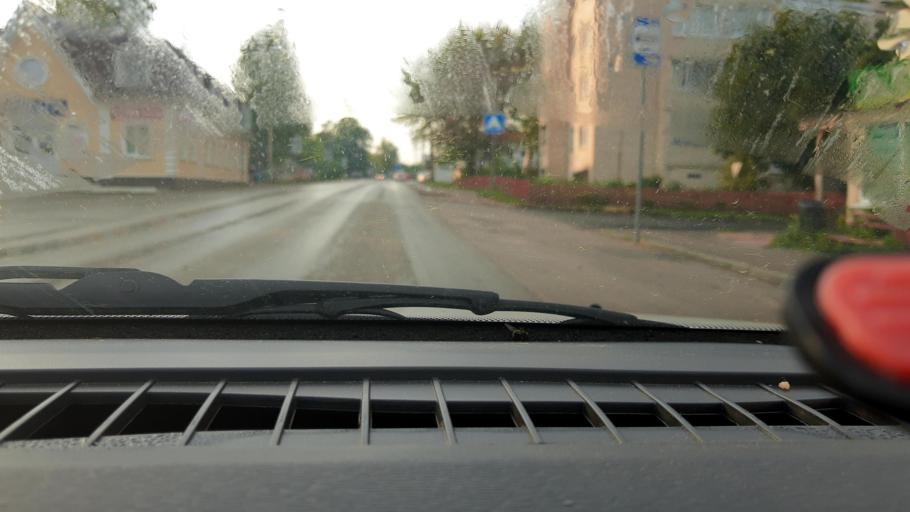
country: RU
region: Nizjnij Novgorod
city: Lukoyanov
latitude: 55.0355
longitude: 44.4946
